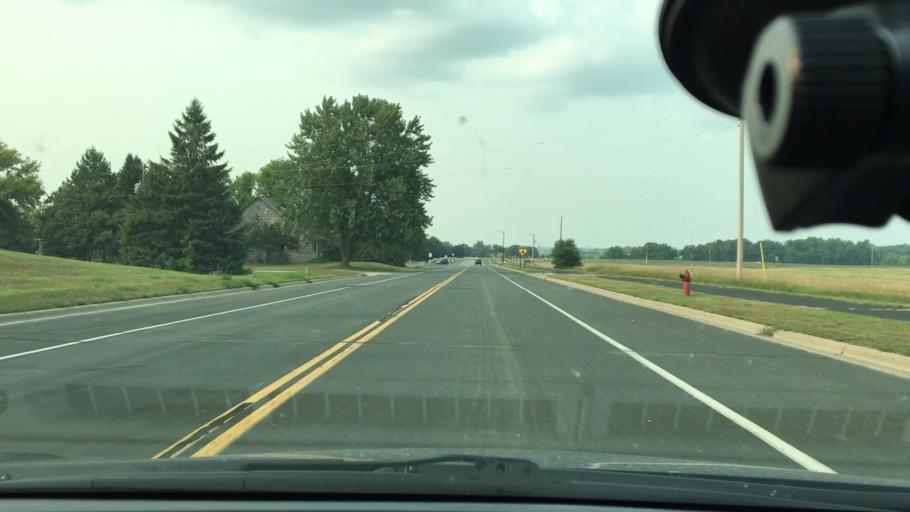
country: US
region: Minnesota
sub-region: Wright County
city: Otsego
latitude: 45.2610
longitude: -93.5606
